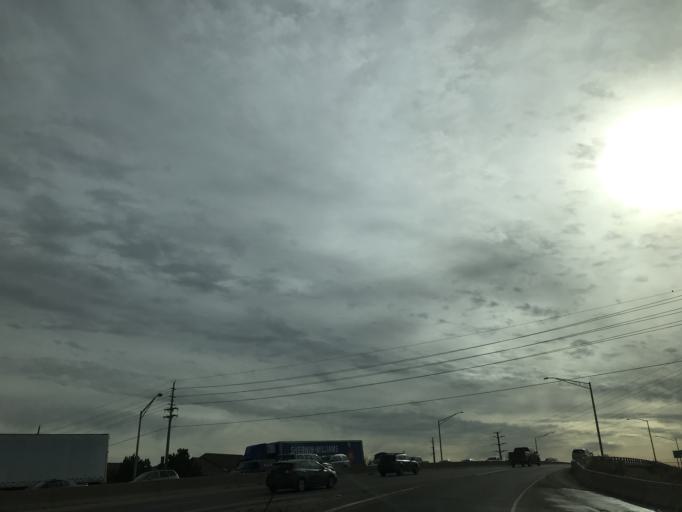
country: US
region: Colorado
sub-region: Adams County
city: Commerce City
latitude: 39.7772
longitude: -104.9038
